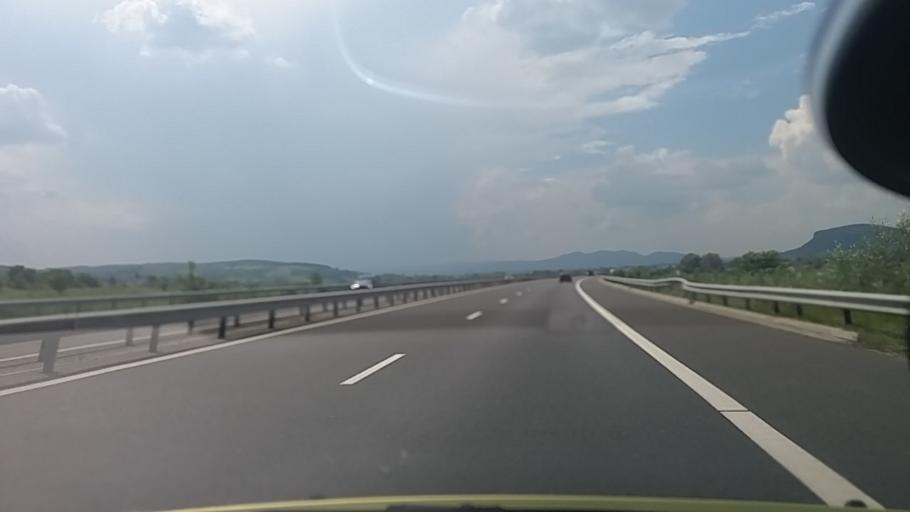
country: RO
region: Hunedoara
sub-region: Comuna Turdas
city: Turdas
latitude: 45.8372
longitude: 23.1011
